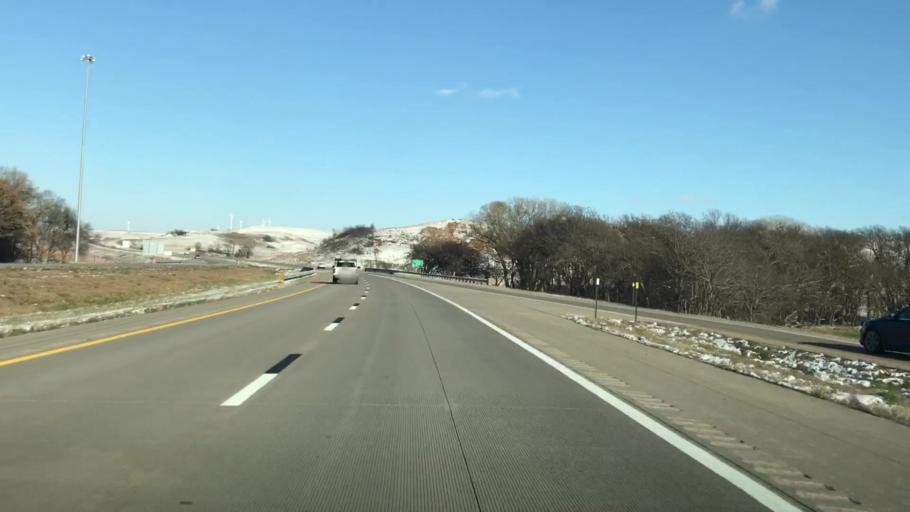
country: US
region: Kansas
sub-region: Ellsworth County
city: Ellsworth
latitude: 38.8593
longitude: -98.1077
